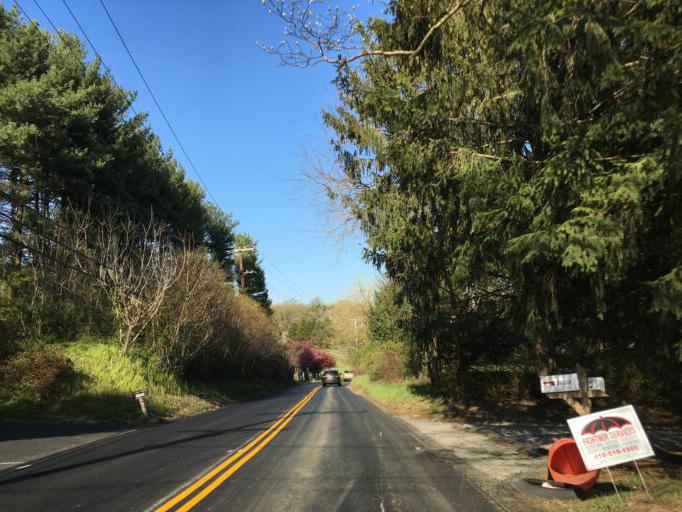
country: US
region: Maryland
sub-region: Baltimore County
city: Hunt Valley
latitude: 39.5197
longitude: -76.5695
